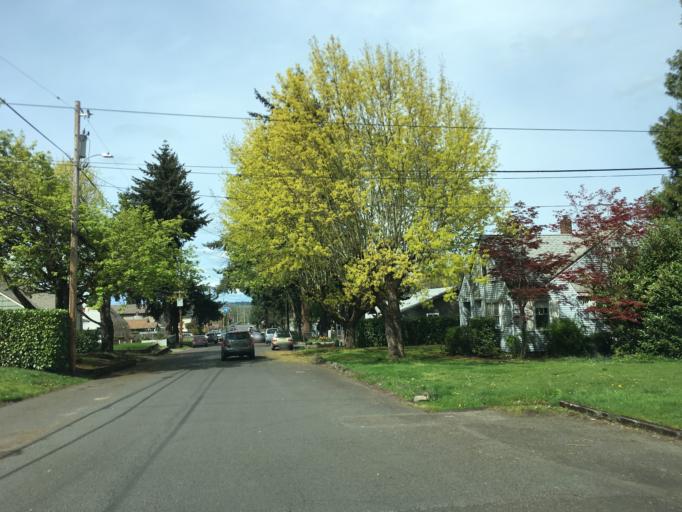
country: US
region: Oregon
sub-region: Multnomah County
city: Lents
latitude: 45.5557
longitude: -122.5628
